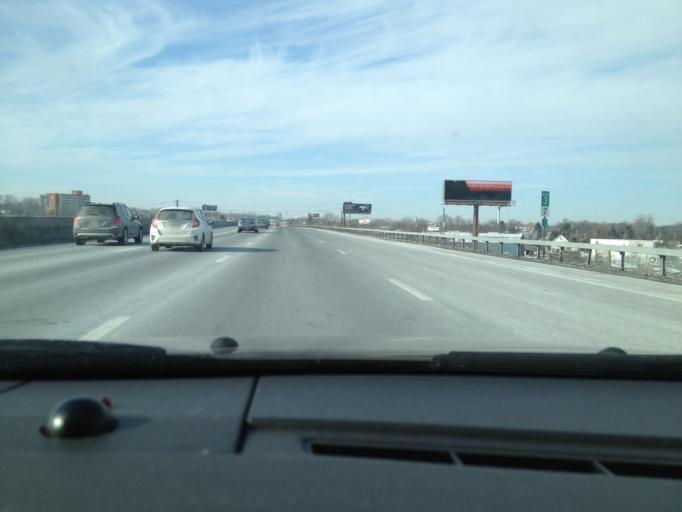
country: US
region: New York
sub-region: Albany County
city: West Albany
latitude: 42.6813
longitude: -73.7749
